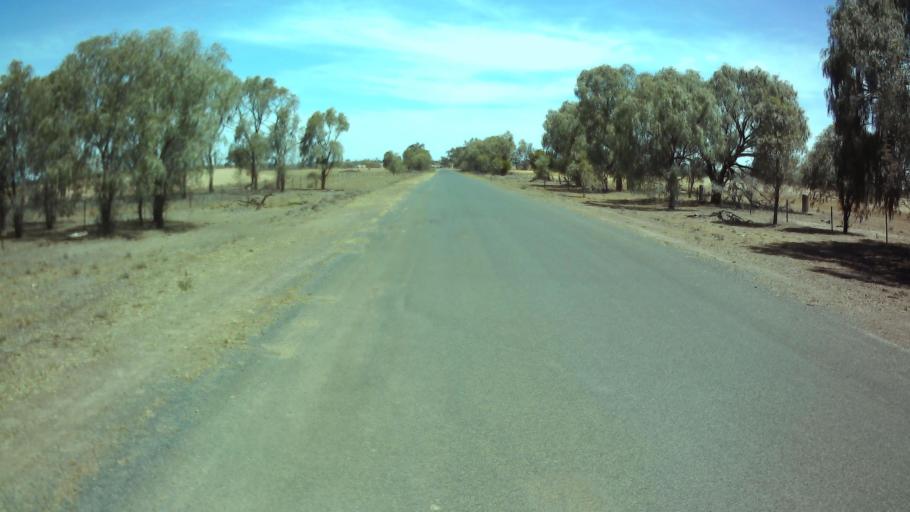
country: AU
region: New South Wales
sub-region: Weddin
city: Grenfell
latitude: -33.8266
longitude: 147.7465
